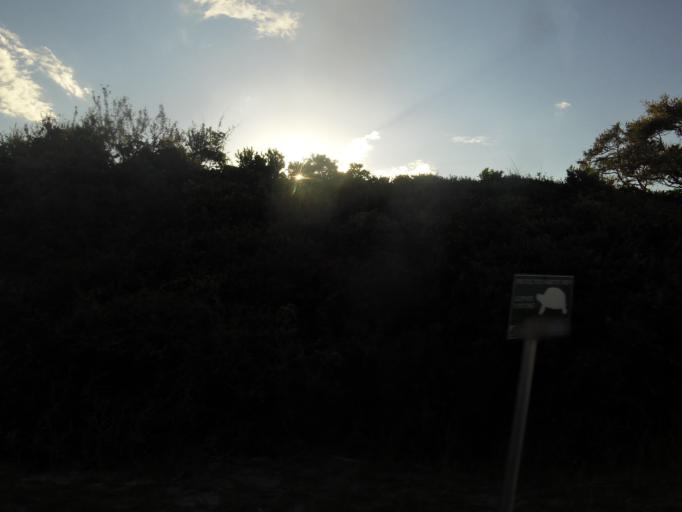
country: US
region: Florida
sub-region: Nassau County
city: Fernandina Beach
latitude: 30.6693
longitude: -81.4331
